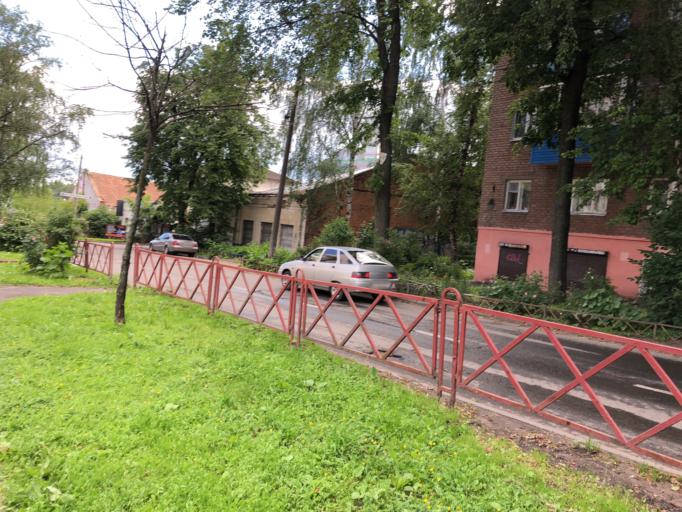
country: RU
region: Jaroslavl
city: Yaroslavl
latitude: 57.6209
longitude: 39.8801
